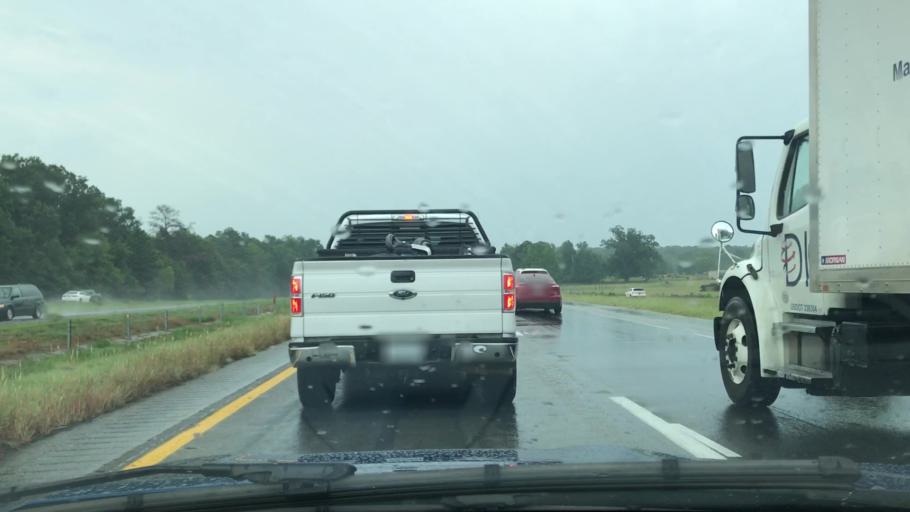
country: US
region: Texas
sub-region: Harrison County
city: Waskom
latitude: 32.4900
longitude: -94.1445
